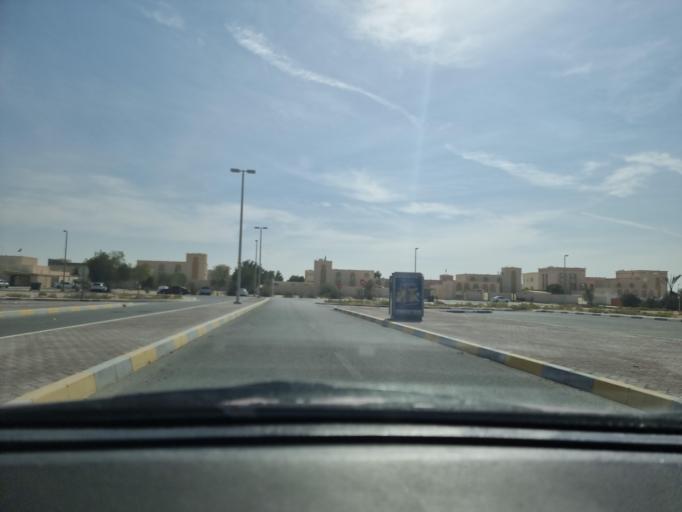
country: AE
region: Abu Dhabi
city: Abu Dhabi
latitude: 24.3849
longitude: 54.6977
